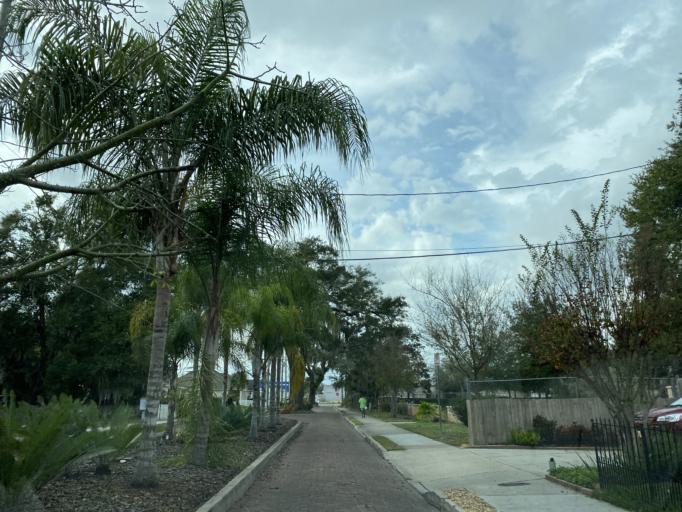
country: US
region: Florida
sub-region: Orange County
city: Orlando
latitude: 28.5521
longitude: -81.3918
